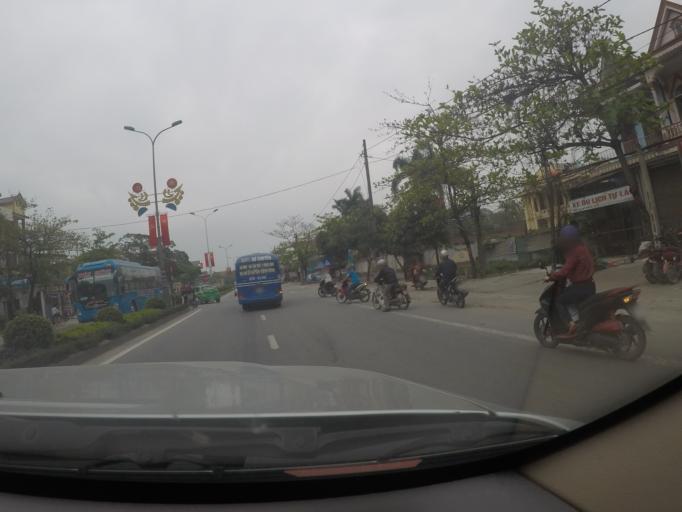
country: VN
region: Nghe An
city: Dien Chau
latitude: 18.9754
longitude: 105.6008
